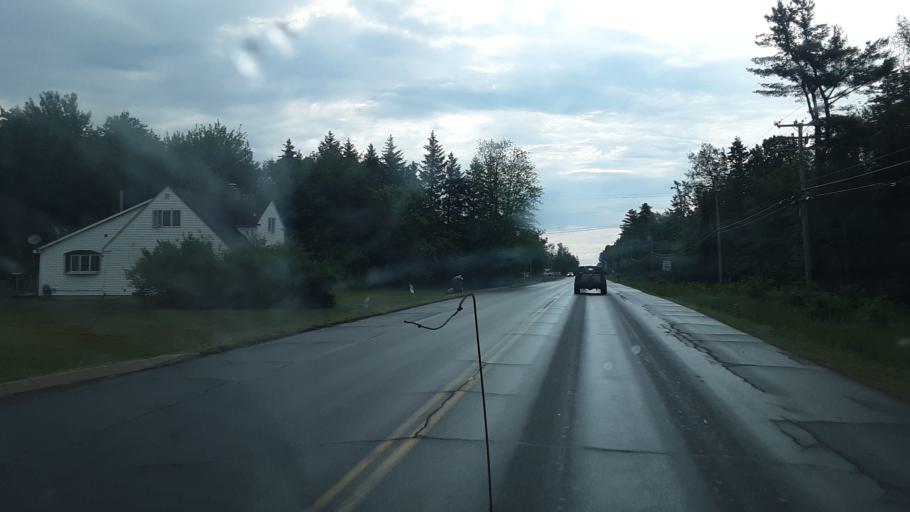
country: US
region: Maine
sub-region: Penobscot County
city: Milford
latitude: 44.9440
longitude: -68.6763
